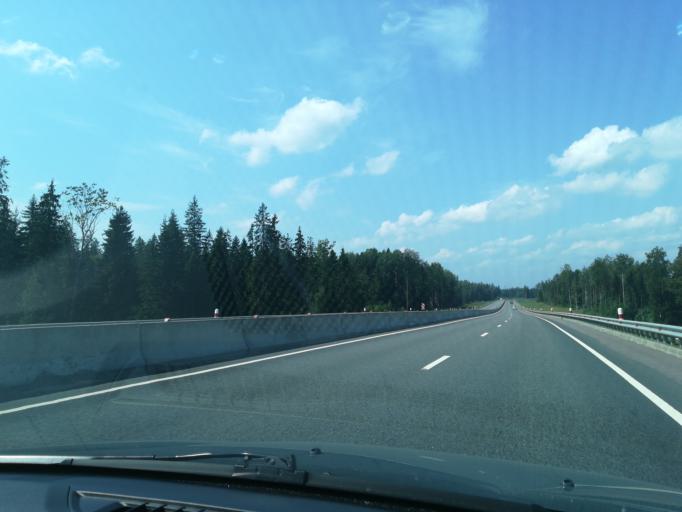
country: RU
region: Leningrad
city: Kingisepp
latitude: 59.5975
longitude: 28.7180
